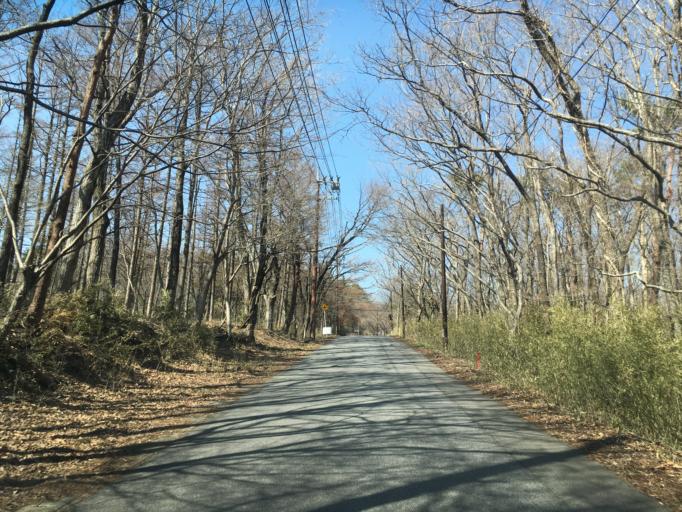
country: JP
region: Tochigi
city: Kuroiso
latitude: 37.0786
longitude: 140.0030
